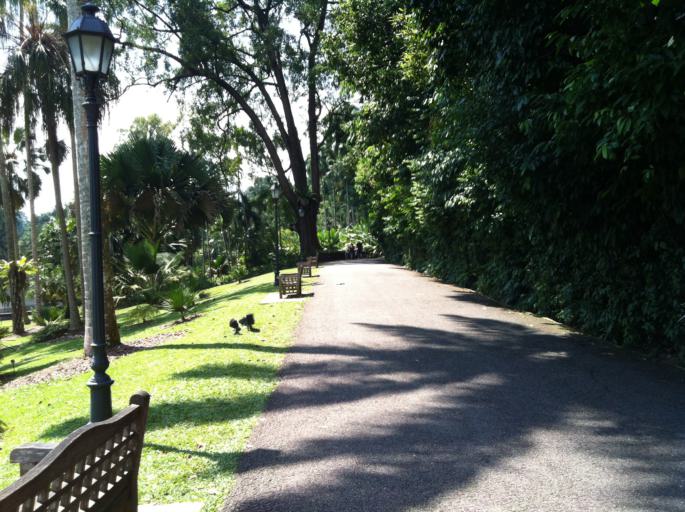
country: SG
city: Singapore
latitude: 1.3125
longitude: 103.8154
